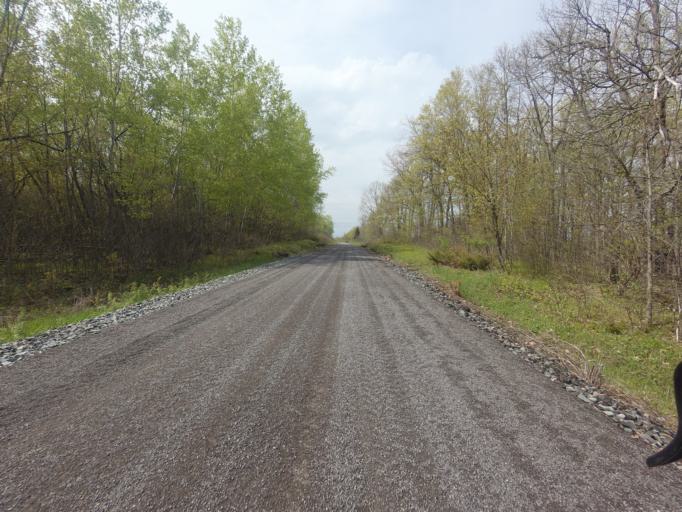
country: CA
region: Ontario
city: Carleton Place
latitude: 45.1614
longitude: -76.1463
